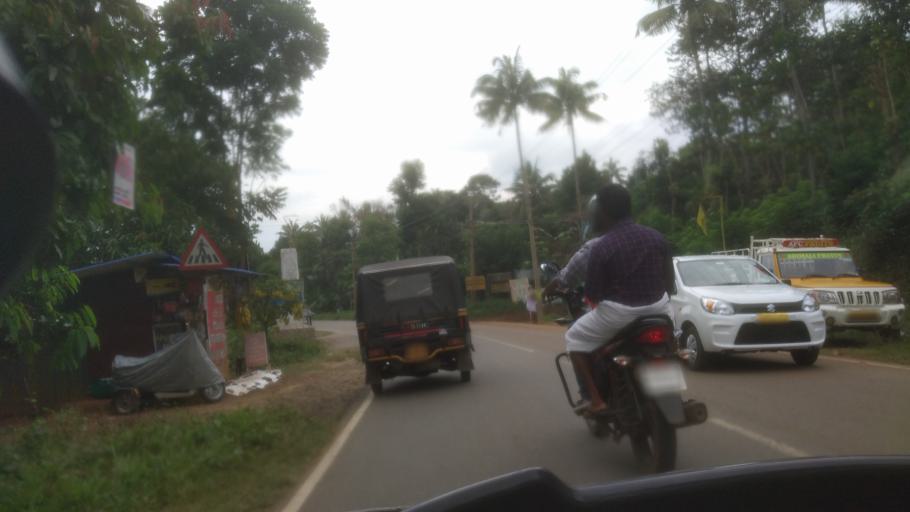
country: IN
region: Kerala
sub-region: Idukki
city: Munnar
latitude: 9.9910
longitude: 76.9811
